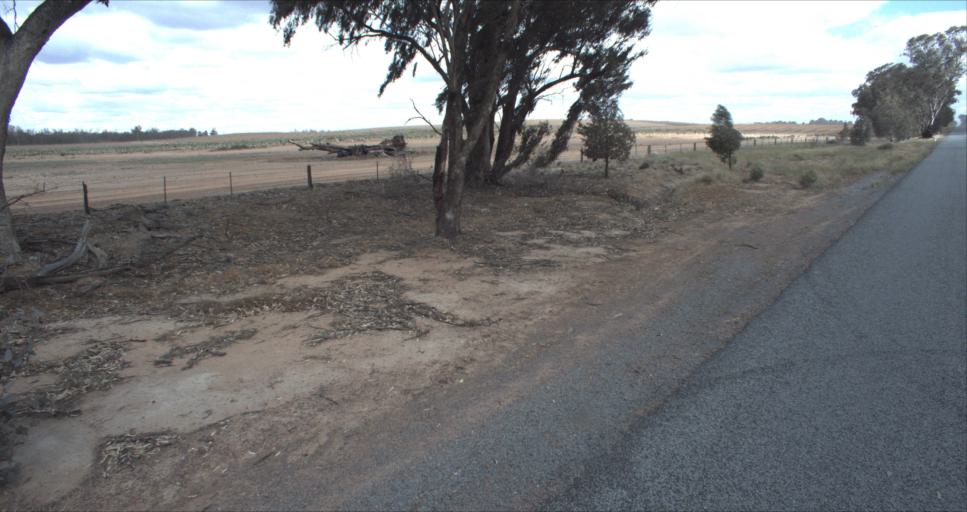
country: AU
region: New South Wales
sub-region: Leeton
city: Leeton
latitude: -34.6528
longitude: 146.3509
